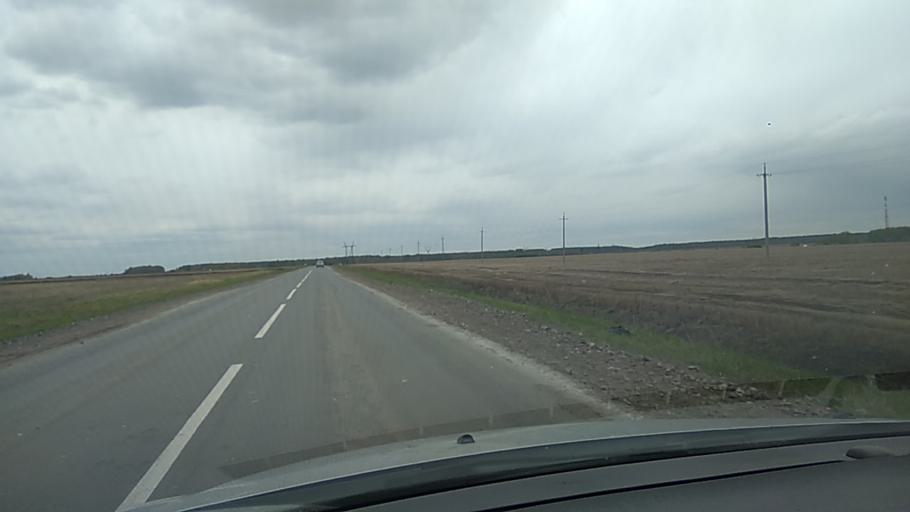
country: RU
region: Sverdlovsk
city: Martyush
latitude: 56.4099
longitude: 61.8067
